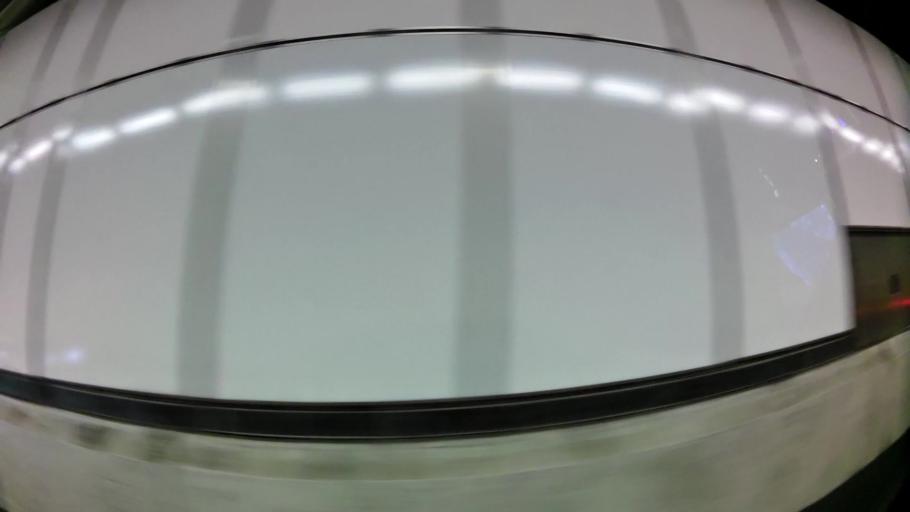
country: HK
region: Kowloon City
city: Kowloon
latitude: 22.2944
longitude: 114.2199
